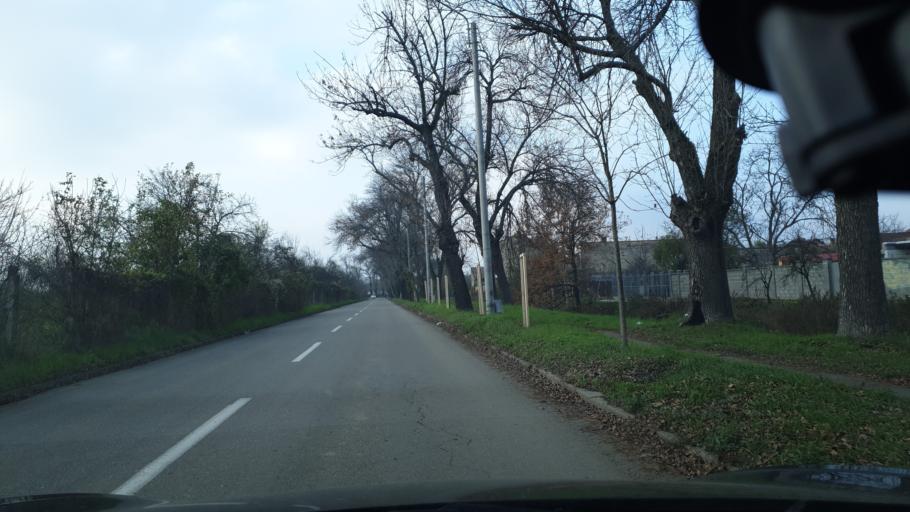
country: RO
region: Timis
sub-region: Comuna Ghiroda
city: Ghiroda
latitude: 45.7591
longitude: 21.2693
